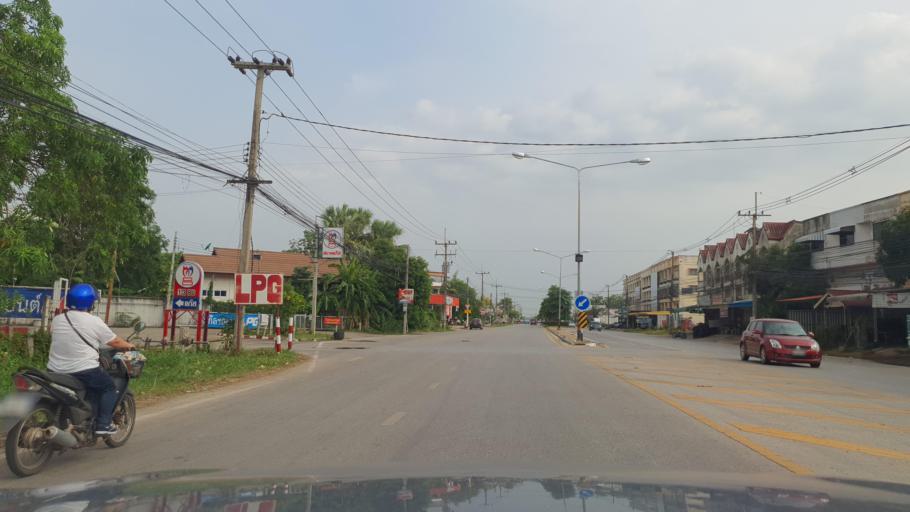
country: TH
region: Phitsanulok
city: Phitsanulok
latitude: 16.8561
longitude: 100.2531
